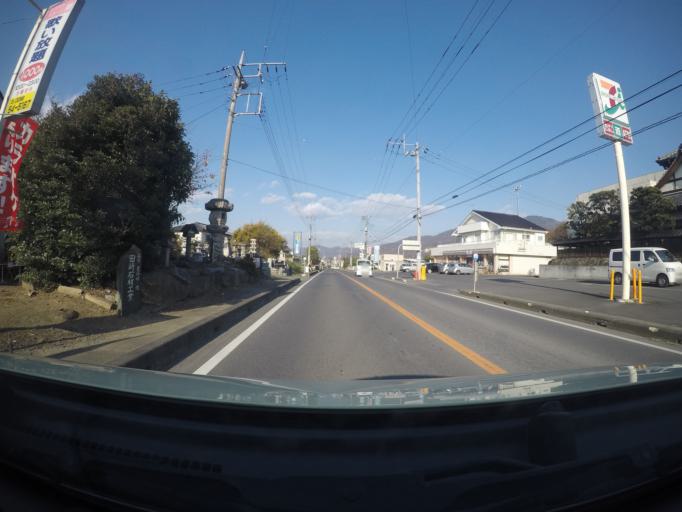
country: JP
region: Ibaraki
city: Makabe
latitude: 36.2752
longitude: 140.1065
